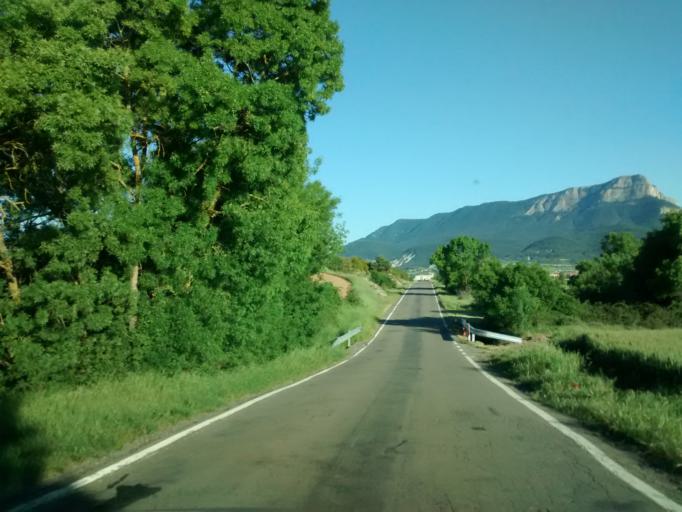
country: ES
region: Aragon
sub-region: Provincia de Huesca
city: Jaca
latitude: 42.5792
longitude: -0.5722
